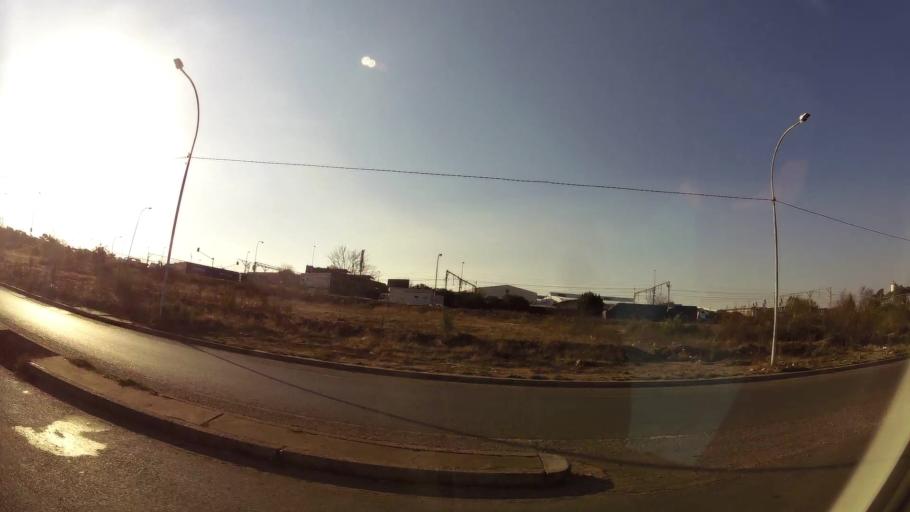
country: ZA
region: Gauteng
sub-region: Ekurhuleni Metropolitan Municipality
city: Germiston
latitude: -26.2101
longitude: 28.1195
